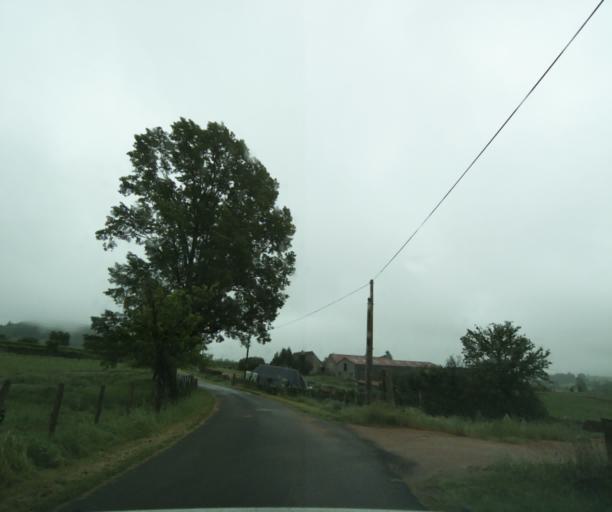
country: FR
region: Bourgogne
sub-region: Departement de Saone-et-Loire
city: Charolles
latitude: 46.3993
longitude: 4.3828
